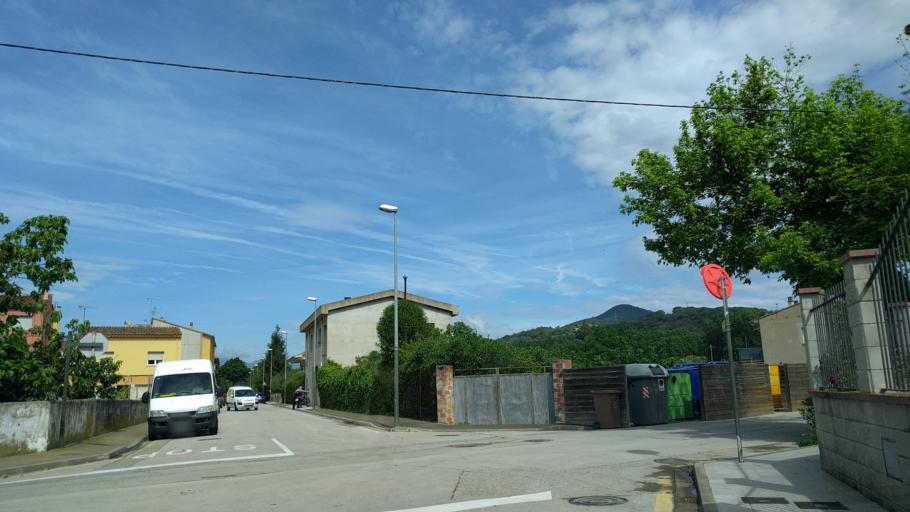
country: ES
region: Catalonia
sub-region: Provincia de Girona
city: Bescano
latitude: 41.9674
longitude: 2.7404
